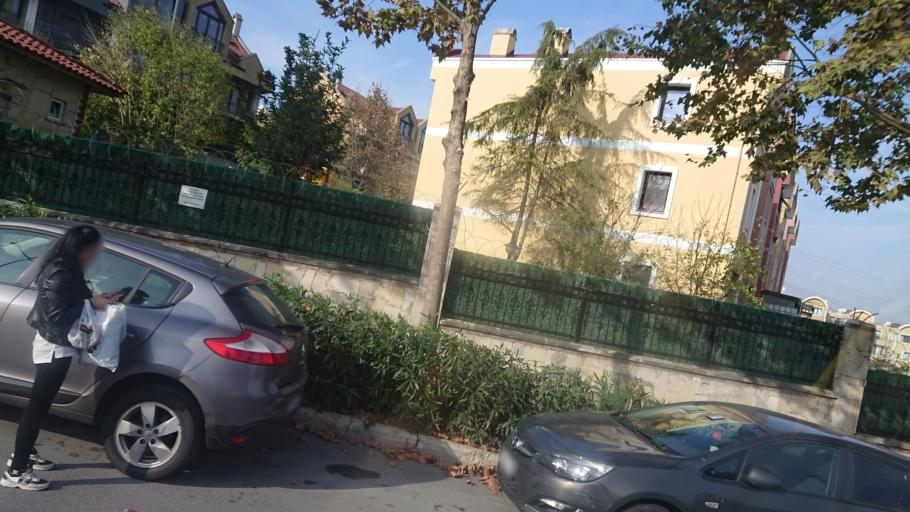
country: TR
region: Istanbul
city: Esenyurt
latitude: 41.0802
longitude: 28.6776
